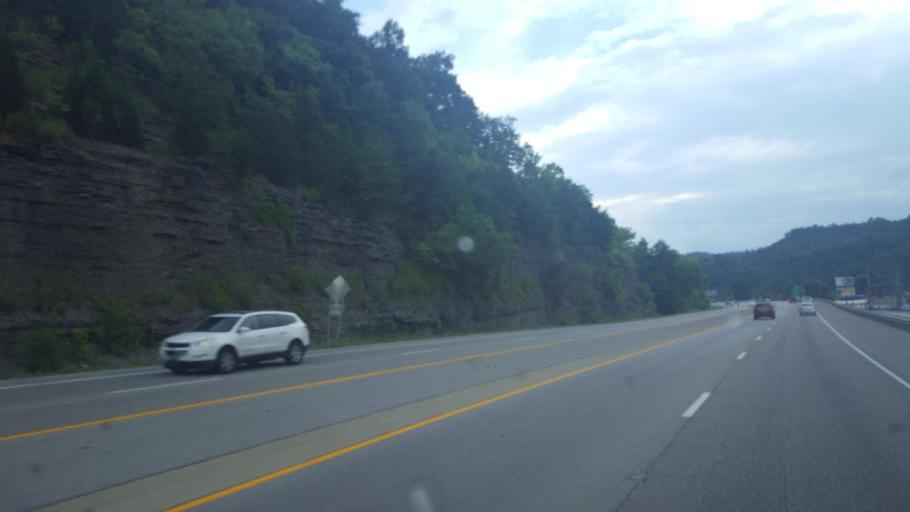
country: US
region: Kentucky
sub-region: Pike County
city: Pikeville
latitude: 37.4905
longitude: -82.5371
